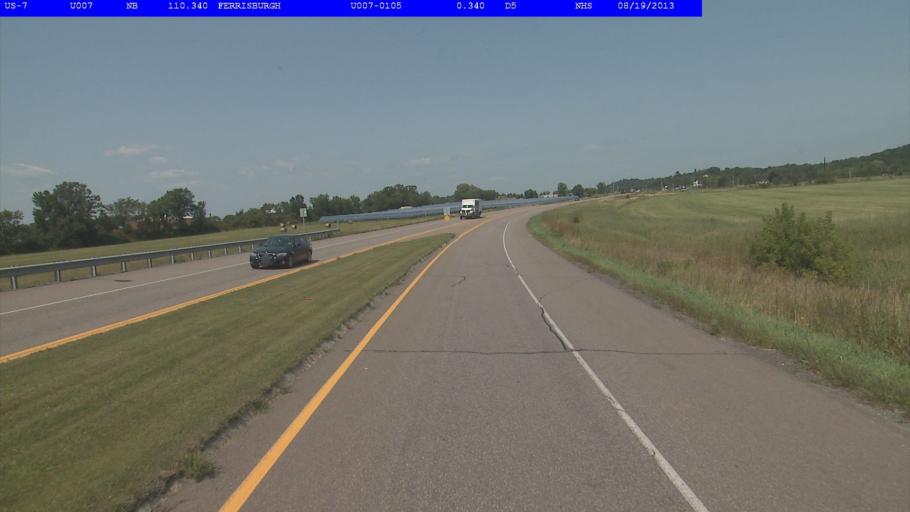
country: US
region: Vermont
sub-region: Addison County
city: Vergennes
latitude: 44.1667
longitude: -73.2390
